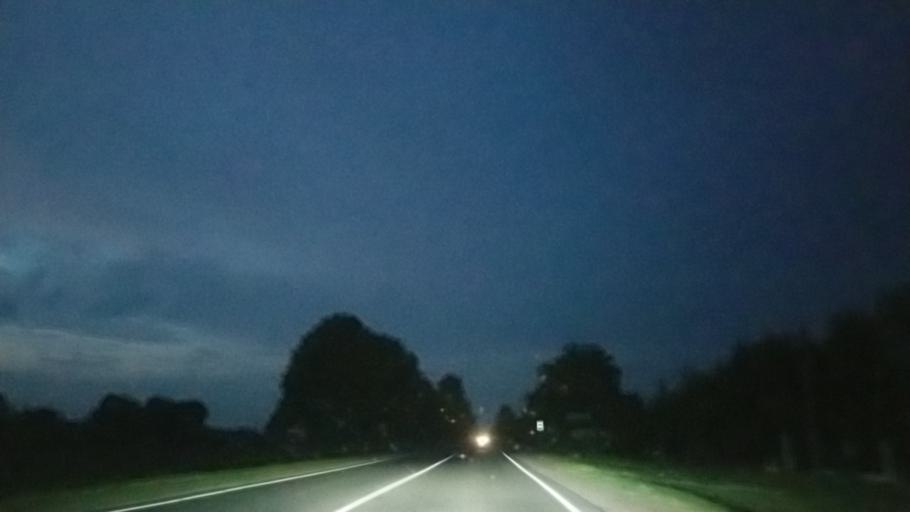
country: PL
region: Lublin Voivodeship
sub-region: Powiat bialski
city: Koden
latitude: 51.9418
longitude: 23.6657
